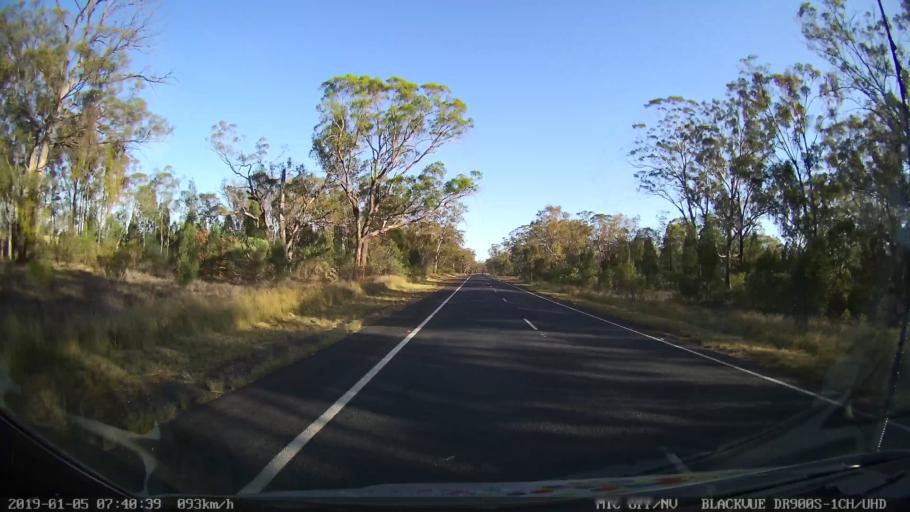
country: AU
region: New South Wales
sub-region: Gilgandra
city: Gilgandra
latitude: -31.9213
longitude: 148.6193
